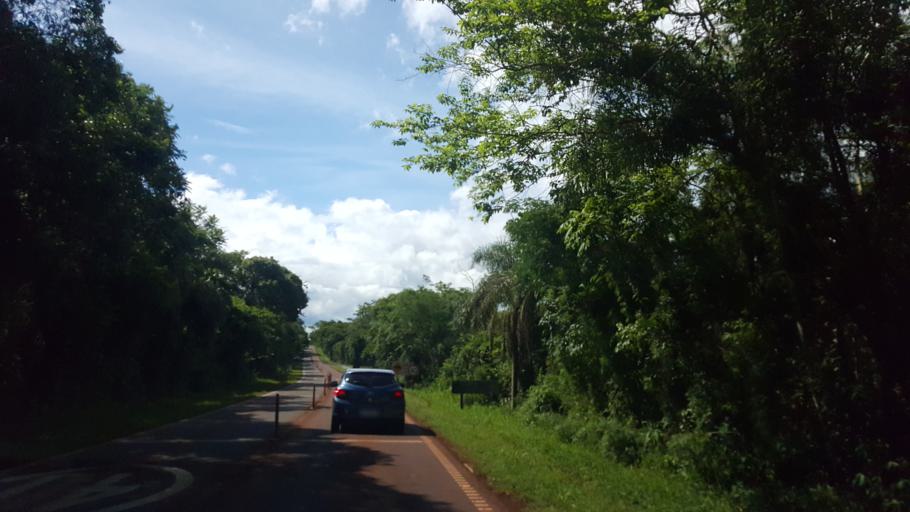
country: AR
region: Misiones
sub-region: Departamento de Iguazu
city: Puerto Iguazu
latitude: -25.6920
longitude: -54.4771
